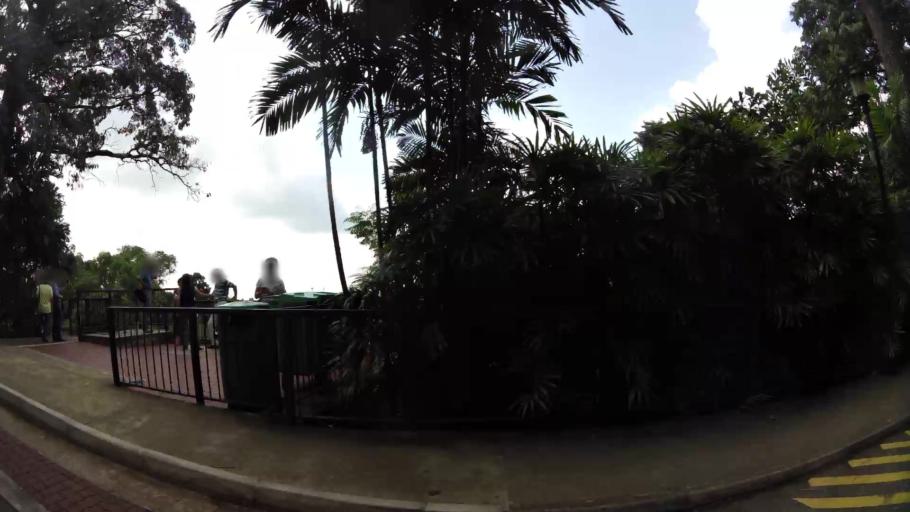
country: SG
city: Singapore
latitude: 1.2730
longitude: 103.8183
